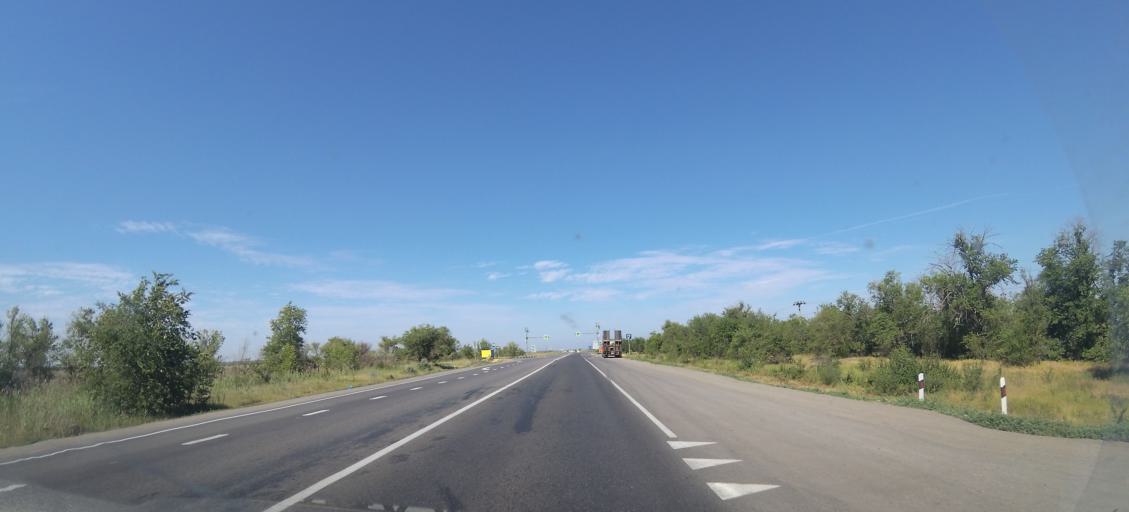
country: RU
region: Volgograd
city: Oktyabr'skiy
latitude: 48.6800
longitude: 43.9074
